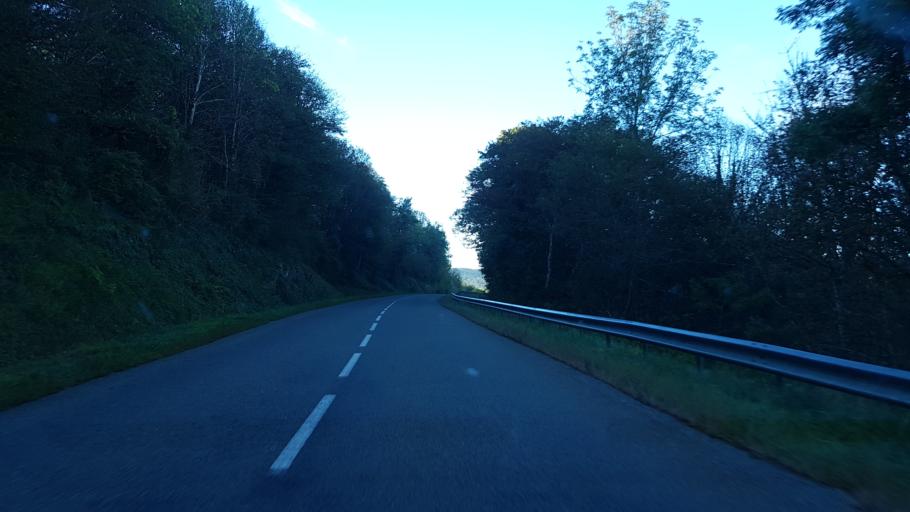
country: FR
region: Franche-Comte
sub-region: Departement du Jura
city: Cousance
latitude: 46.5509
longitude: 5.4868
